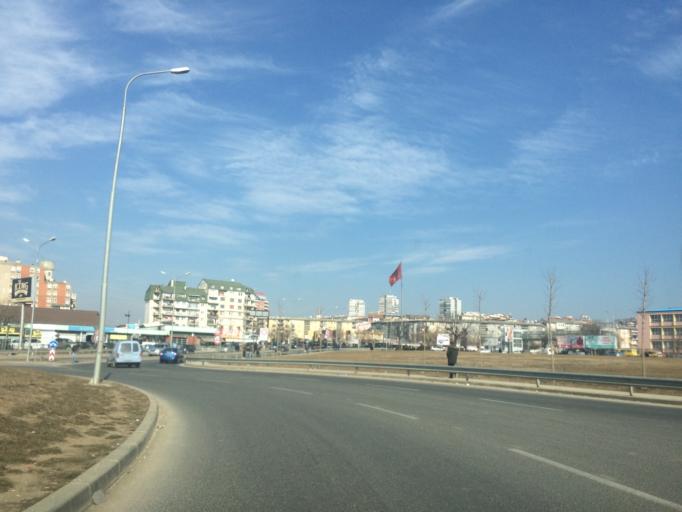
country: XK
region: Pristina
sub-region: Komuna e Prishtines
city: Pristina
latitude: 42.6463
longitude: 21.1558
